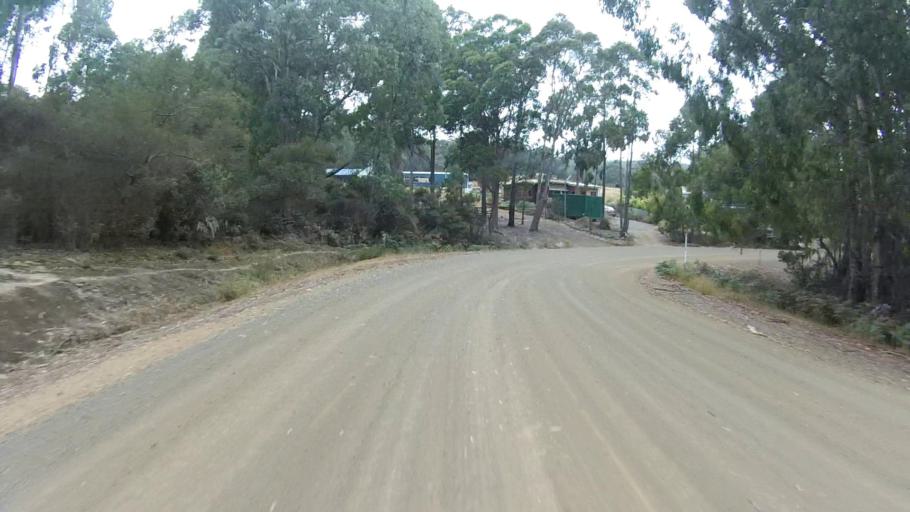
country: AU
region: Tasmania
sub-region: Huon Valley
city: Cygnet
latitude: -43.2246
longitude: 147.0967
